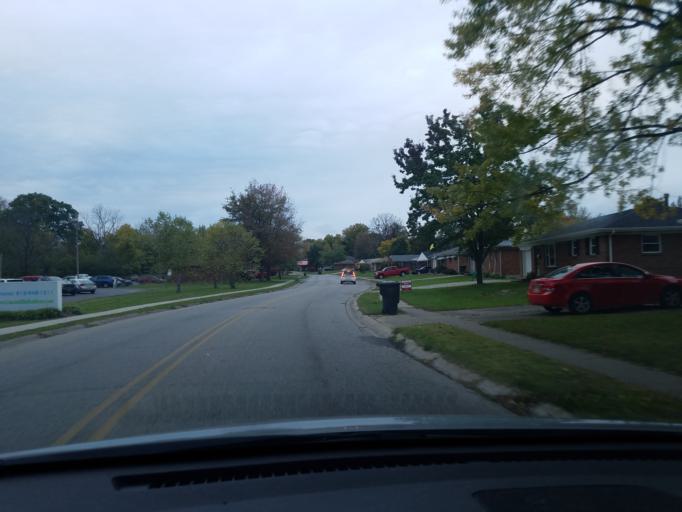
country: US
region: Indiana
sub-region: Floyd County
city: New Albany
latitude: 38.3042
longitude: -85.8298
